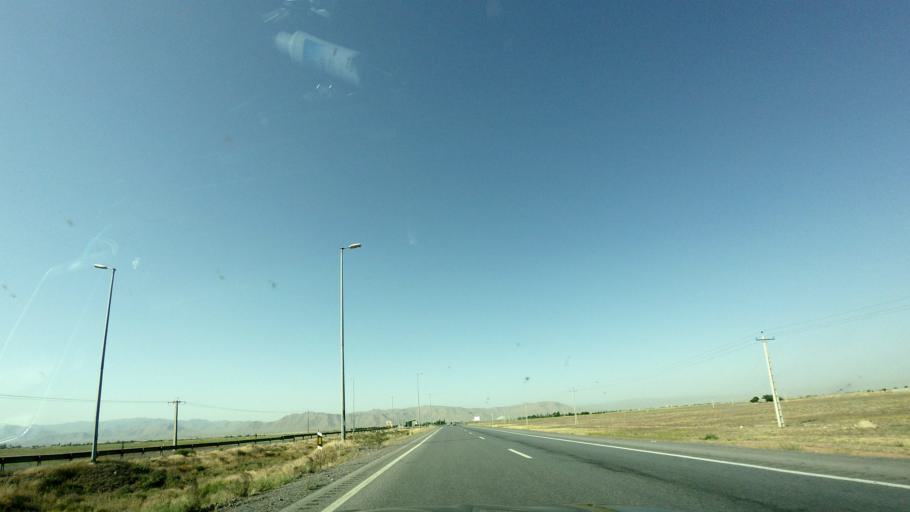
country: IR
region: Markazi
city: Ashtian
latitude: 34.1912
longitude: 50.0546
